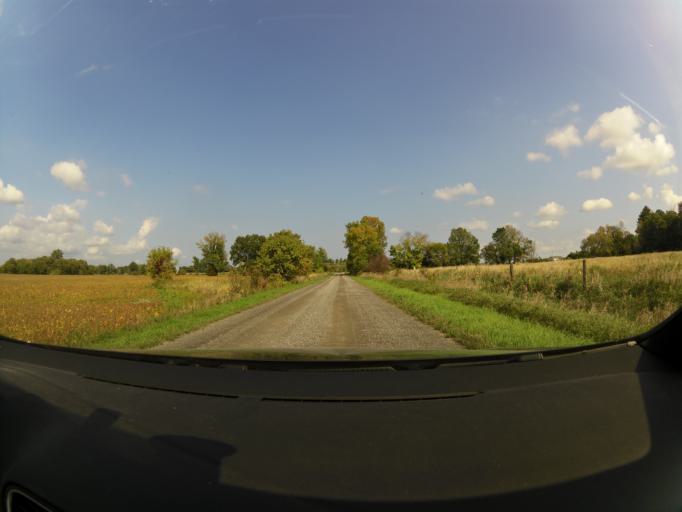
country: CA
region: Ontario
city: Arnprior
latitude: 45.4084
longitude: -76.2398
